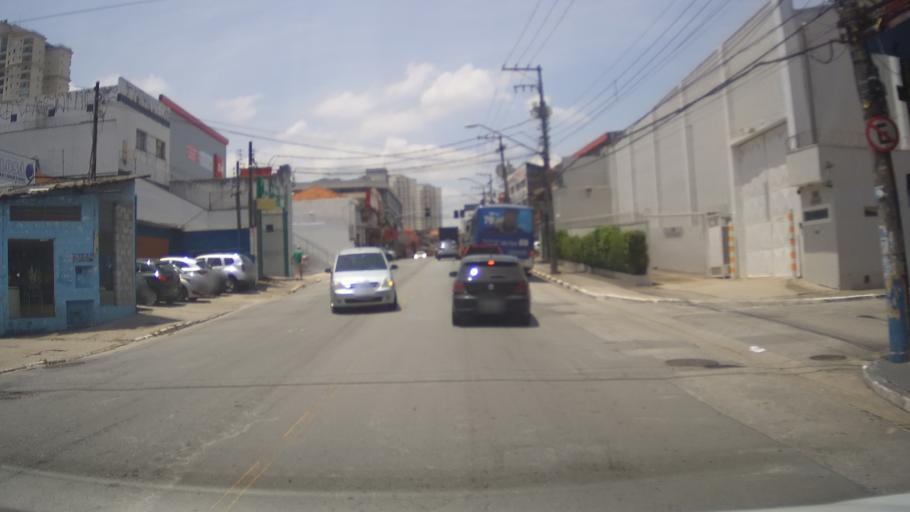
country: BR
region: Sao Paulo
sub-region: Guarulhos
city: Guarulhos
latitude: -23.4828
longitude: -46.5421
